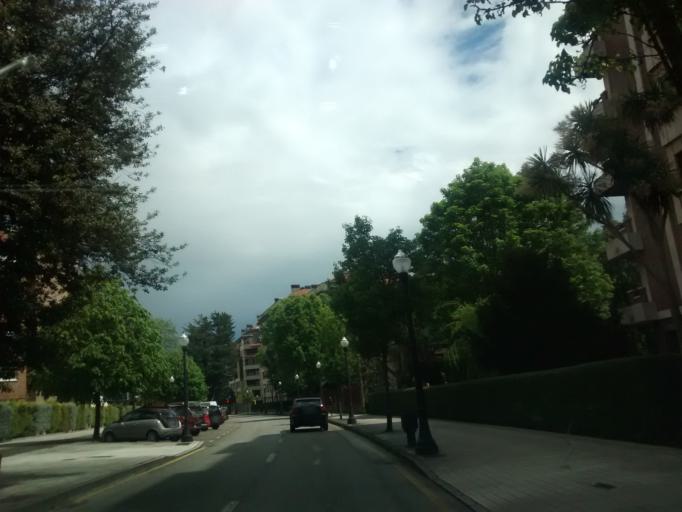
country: ES
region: Asturias
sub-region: Province of Asturias
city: Gijon
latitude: 43.5340
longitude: -5.6423
